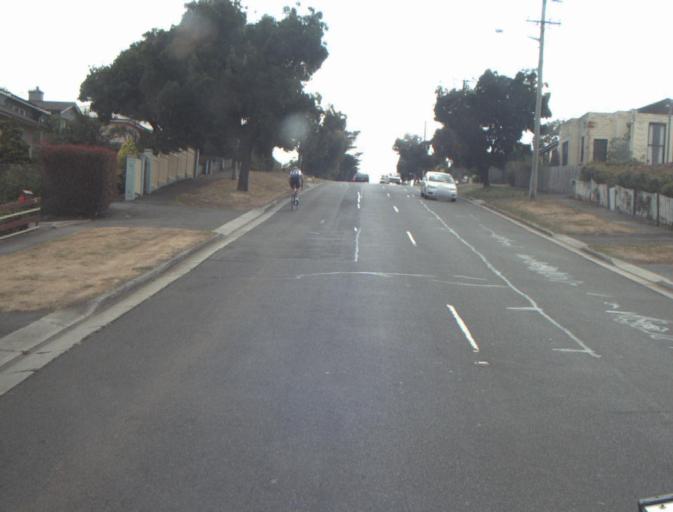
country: AU
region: Tasmania
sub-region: Launceston
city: East Launceston
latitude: -41.4741
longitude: 147.1667
